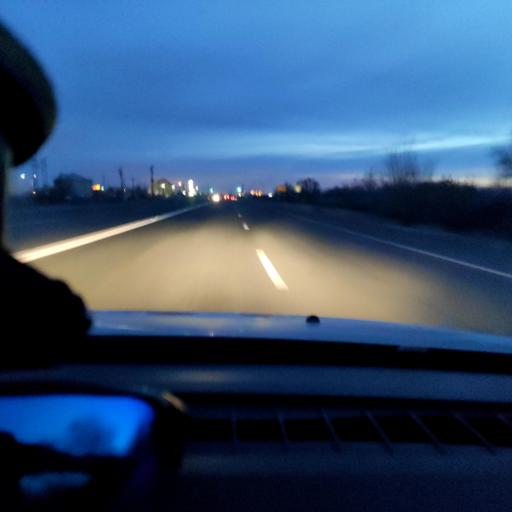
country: RU
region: Samara
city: Novokuybyshevsk
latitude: 53.0678
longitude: 50.0256
